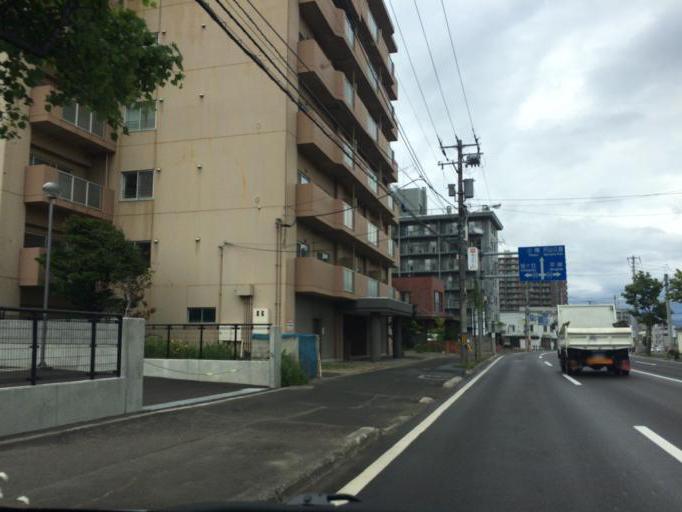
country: JP
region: Hokkaido
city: Sapporo
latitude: 43.0325
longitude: 141.3354
